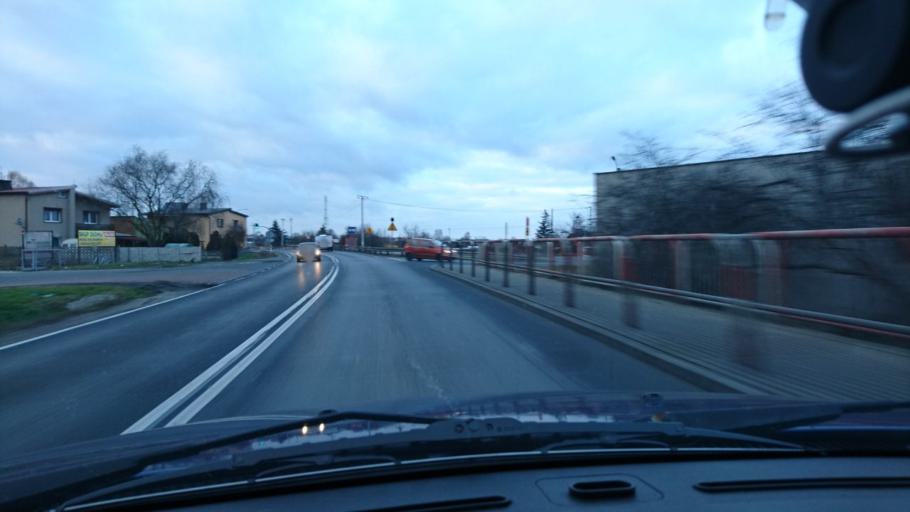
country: PL
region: Greater Poland Voivodeship
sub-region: Powiat kepinski
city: Baranow
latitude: 51.2680
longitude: 17.9984
